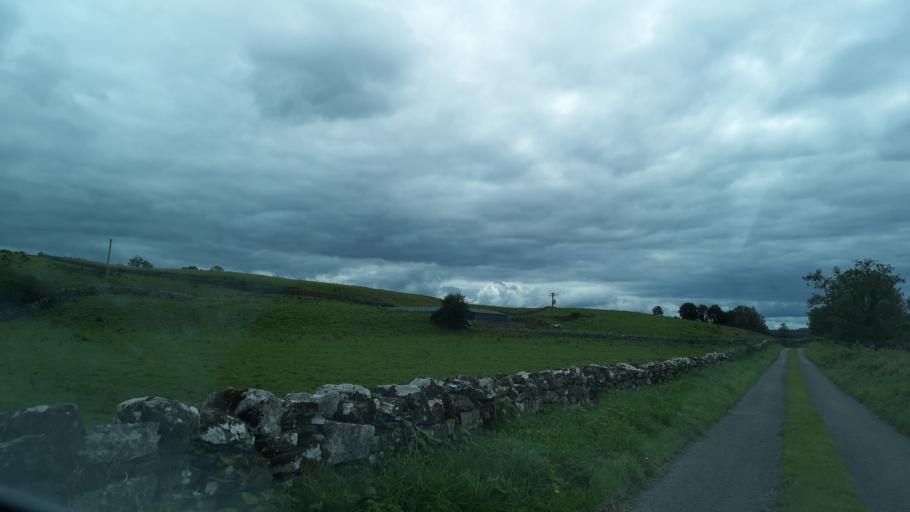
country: IE
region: Connaught
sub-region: County Galway
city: Loughrea
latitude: 53.1639
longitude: -8.4536
